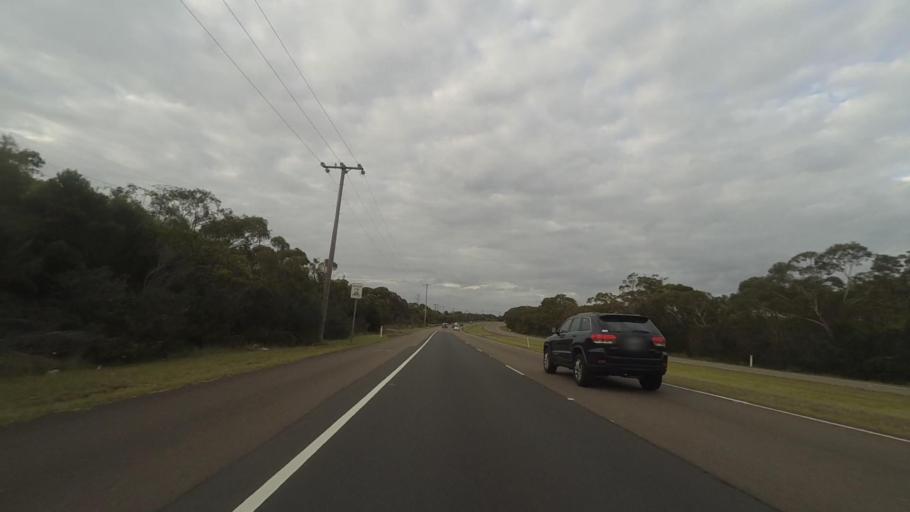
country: AU
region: New South Wales
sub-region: Sutherland Shire
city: Heathcote
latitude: -34.1171
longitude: 150.9916
